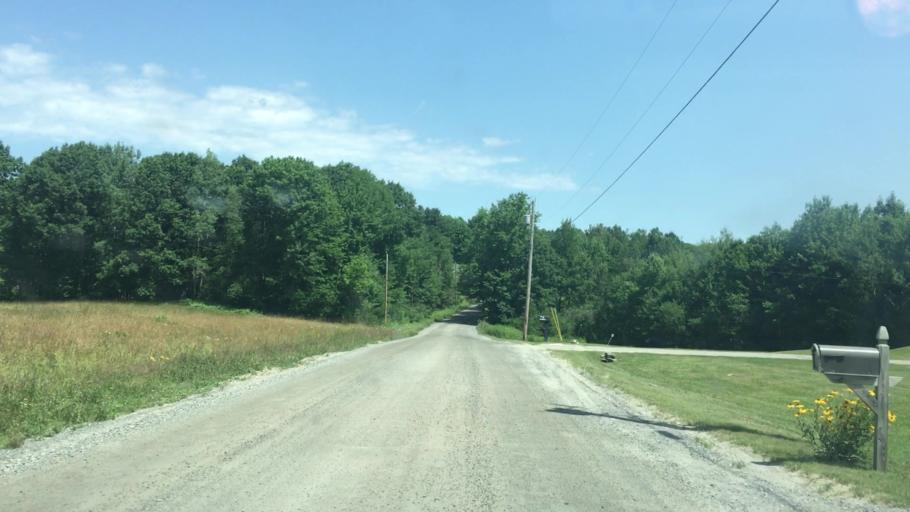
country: US
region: Maine
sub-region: Kennebec County
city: Monmouth
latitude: 44.2832
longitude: -70.0573
